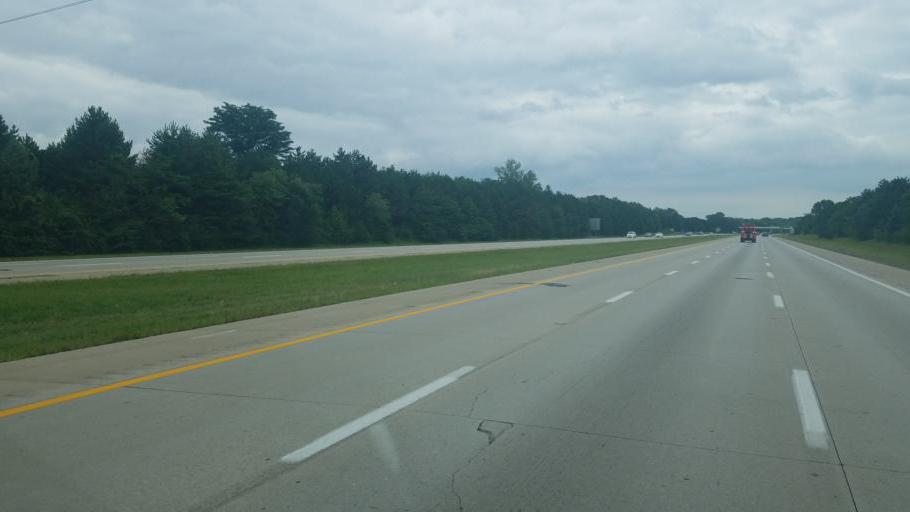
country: US
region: Ohio
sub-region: Franklin County
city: Grove City
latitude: 39.9011
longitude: -83.0646
